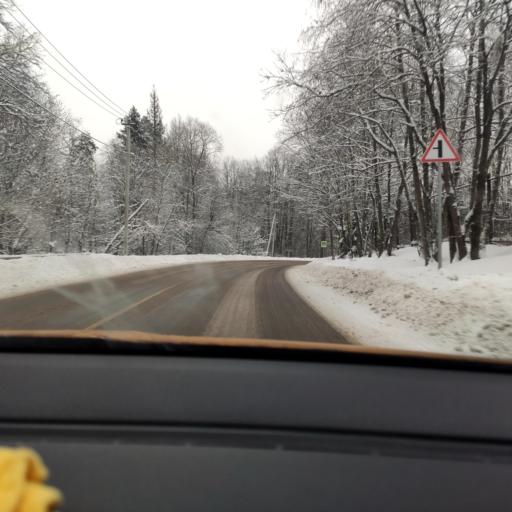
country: RU
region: Moskovskaya
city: Yershovo
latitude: 55.7729
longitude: 36.7968
